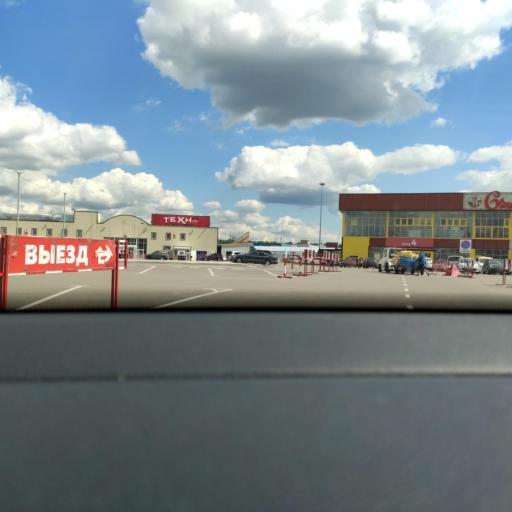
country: RU
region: Moscow
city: Lyublino
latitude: 55.6749
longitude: 37.7767
